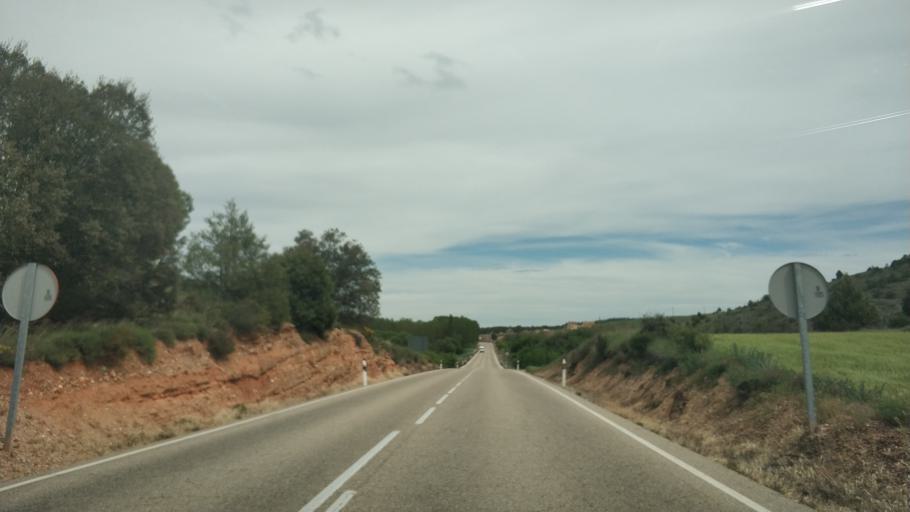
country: ES
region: Castille and Leon
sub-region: Provincia de Soria
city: El Burgo de Osma
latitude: 41.5737
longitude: -3.0182
